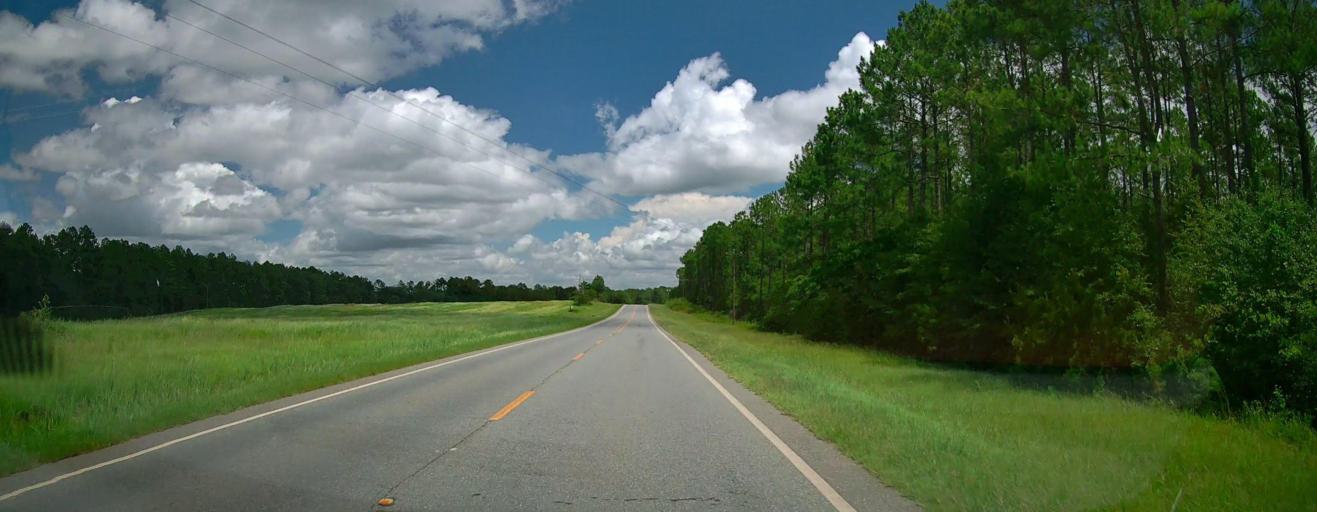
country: US
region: Georgia
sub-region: Turner County
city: Ashburn
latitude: 31.7197
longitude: -83.5960
